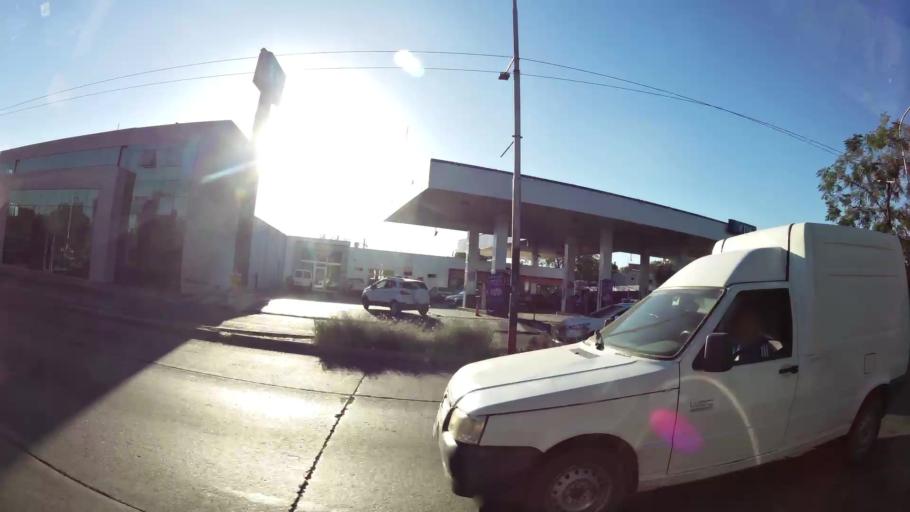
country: AR
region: Mendoza
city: Mendoza
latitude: -32.8796
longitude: -68.8269
